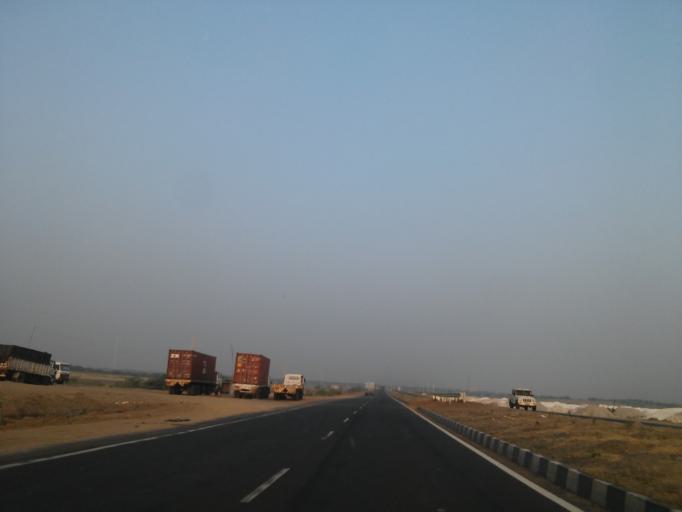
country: IN
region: Gujarat
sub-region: Kachchh
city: Bhachau
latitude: 23.2476
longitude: 70.6641
